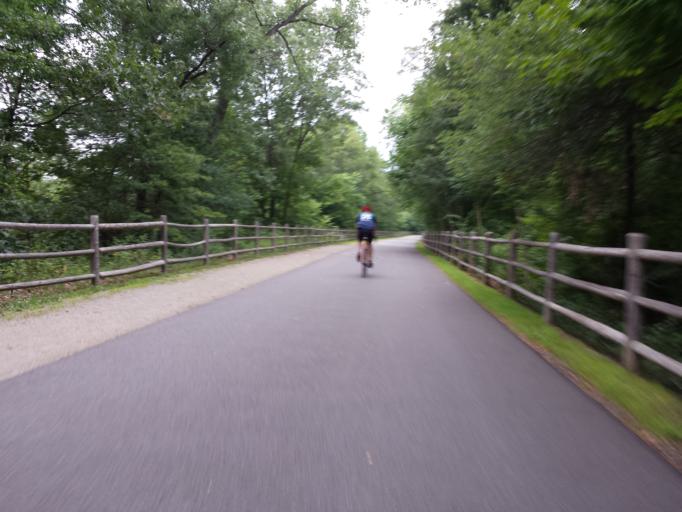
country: US
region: New York
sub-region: Dutchess County
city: Myers Corner
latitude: 41.6255
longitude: -73.8538
